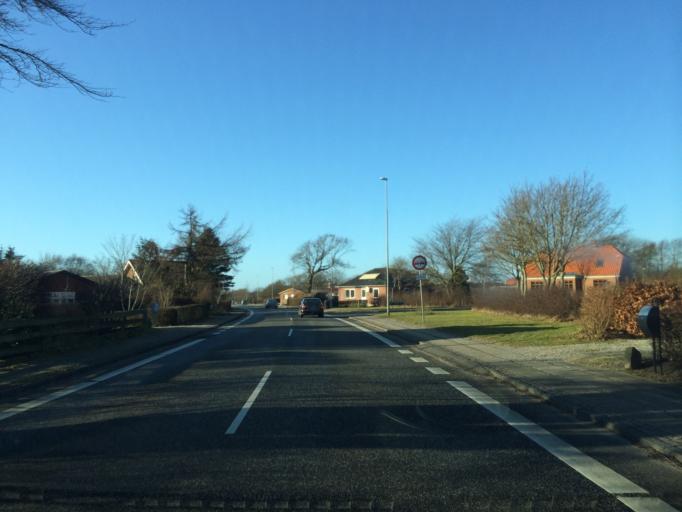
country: DK
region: Central Jutland
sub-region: Ringkobing-Skjern Kommune
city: Ringkobing
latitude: 56.1100
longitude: 8.3187
